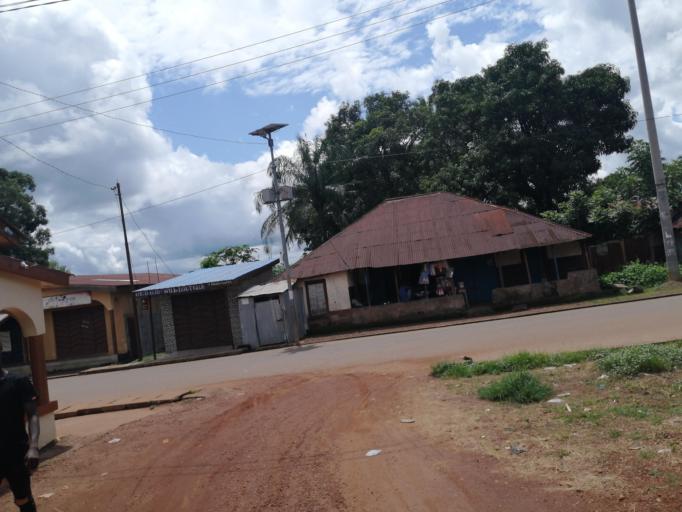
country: SL
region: Northern Province
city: Port Loko
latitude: 8.7658
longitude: -12.7869
